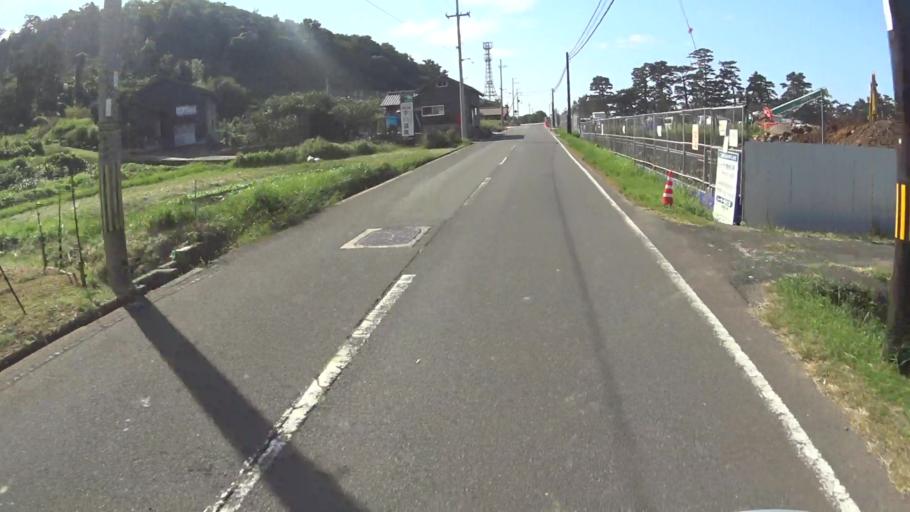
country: JP
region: Kyoto
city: Miyazu
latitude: 35.7642
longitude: 135.1965
